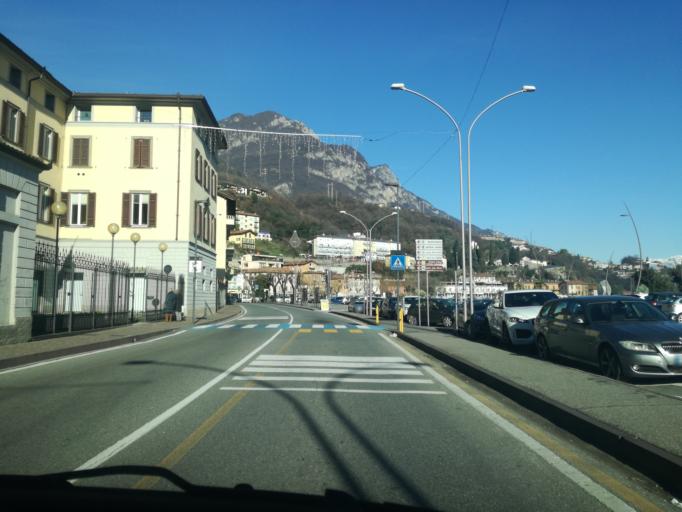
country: IT
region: Lombardy
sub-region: Provincia di Bergamo
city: Lovere
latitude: 45.8193
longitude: 10.0794
